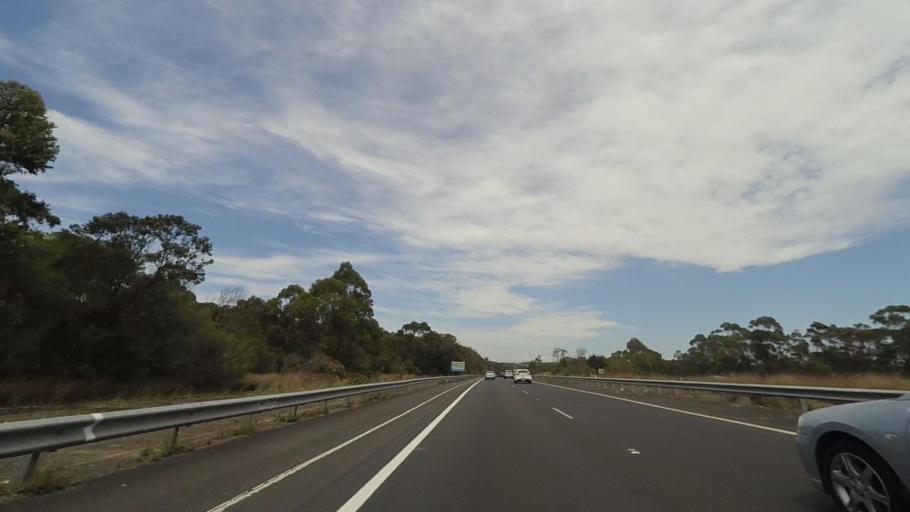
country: AU
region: New South Wales
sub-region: Wollongong
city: Helensburgh
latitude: -34.1504
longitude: 150.9904
